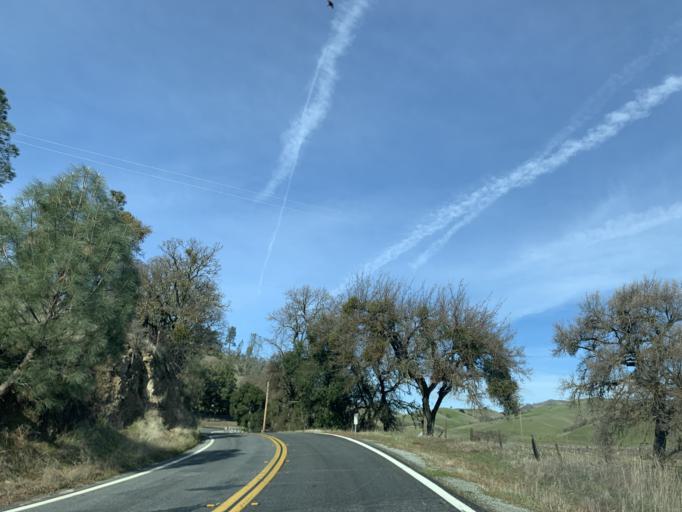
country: US
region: California
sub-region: Monterey County
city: Soledad
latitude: 36.5453
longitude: -121.1567
